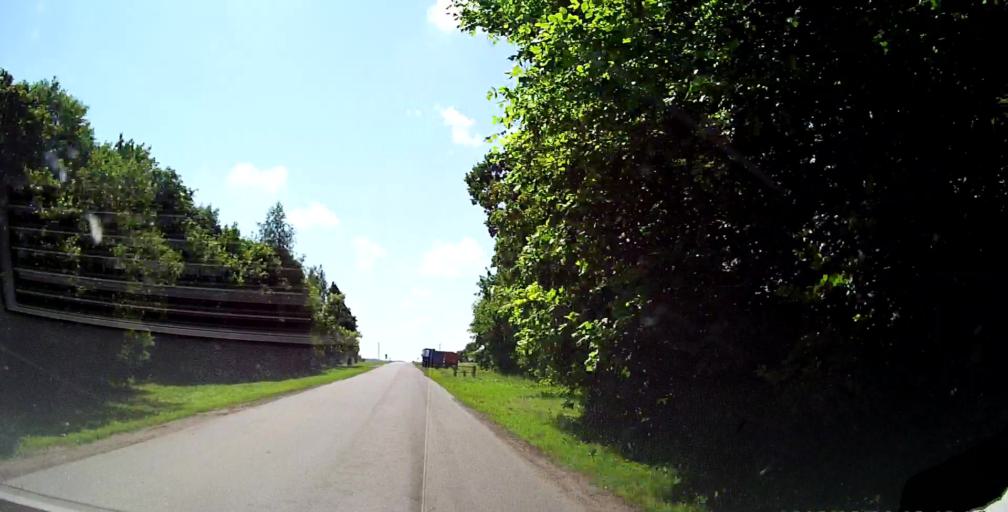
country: RU
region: Lipetsk
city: Chaplygin
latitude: 53.3196
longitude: 39.9574
